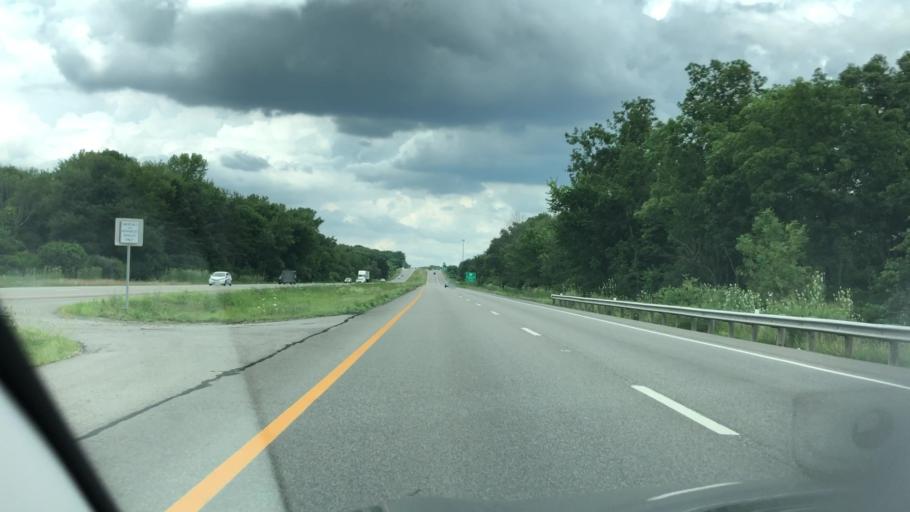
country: US
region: Ohio
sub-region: Summit County
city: Norton
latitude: 41.0877
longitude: -81.6608
